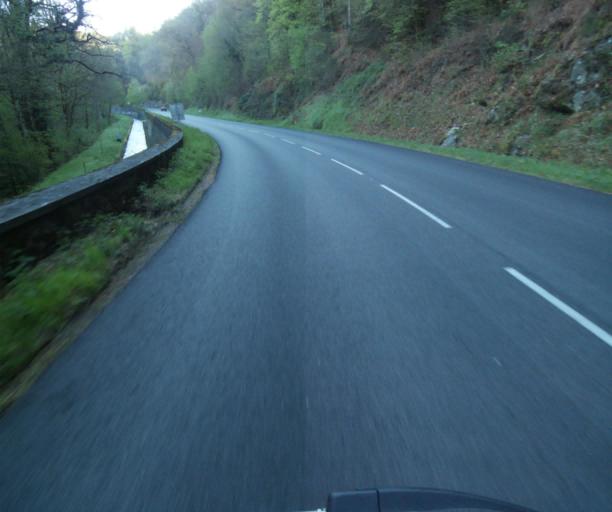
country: FR
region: Limousin
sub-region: Departement de la Correze
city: Correze
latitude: 45.3624
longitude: 1.8763
